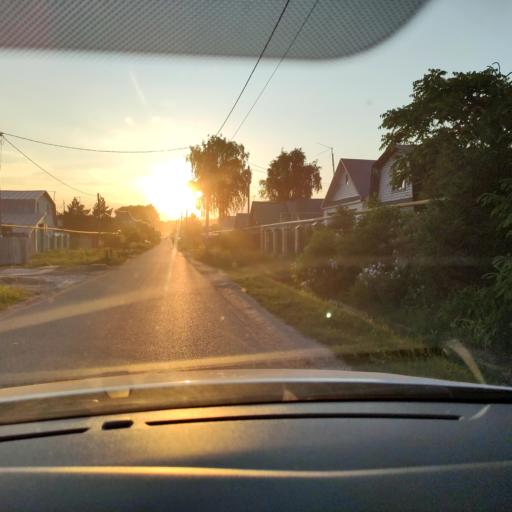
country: RU
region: Tatarstan
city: Stolbishchi
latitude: 55.7480
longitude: 49.3029
